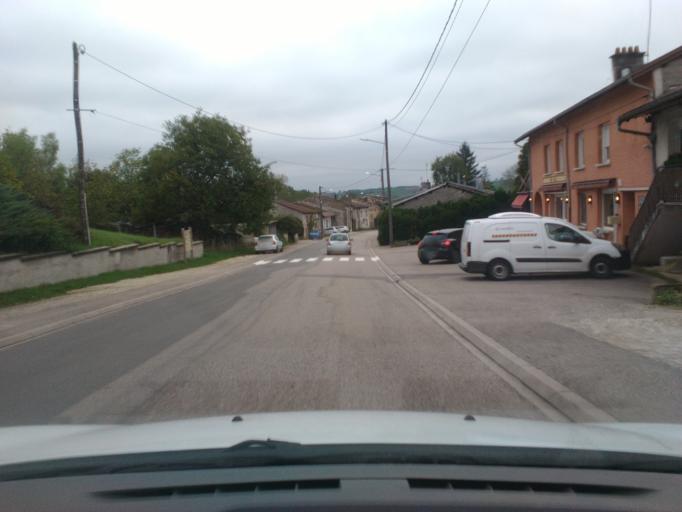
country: FR
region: Lorraine
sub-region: Departement des Vosges
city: Vincey
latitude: 48.3003
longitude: 6.3092
